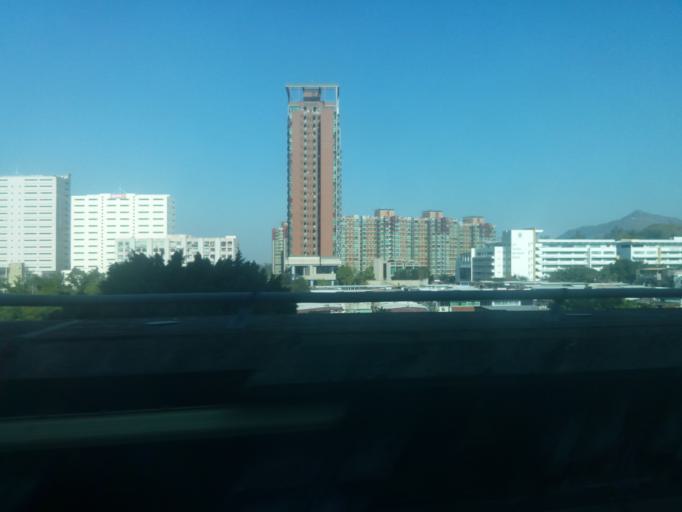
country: HK
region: Yuen Long
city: Yuen Long Kau Hui
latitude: 22.4475
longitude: 114.0300
